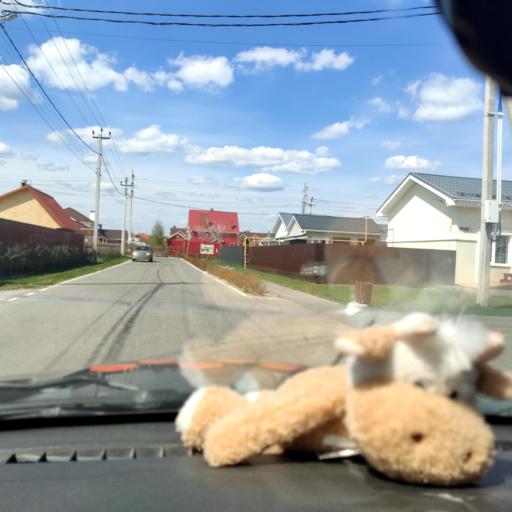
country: RU
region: Samara
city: Podstepki
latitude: 53.5762
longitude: 49.0838
